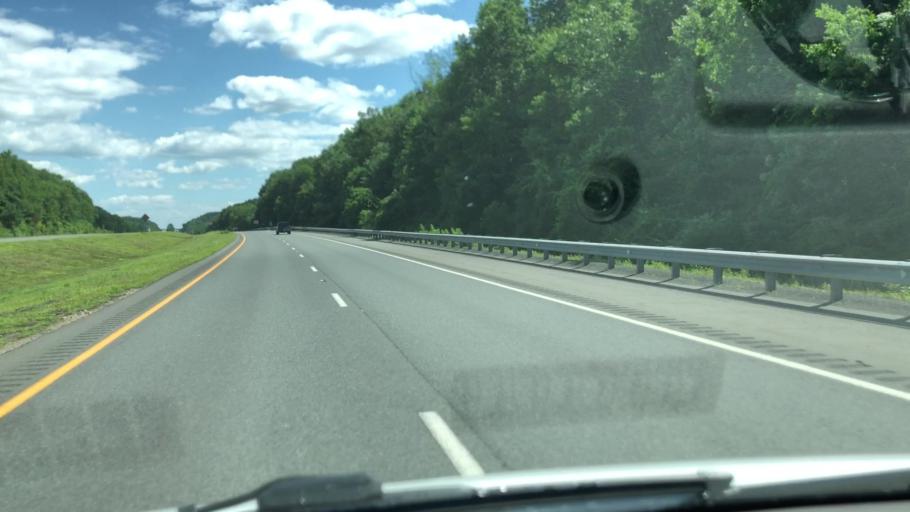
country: US
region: Massachusetts
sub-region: Franklin County
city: South Deerfield
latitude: 42.5303
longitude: -72.6281
